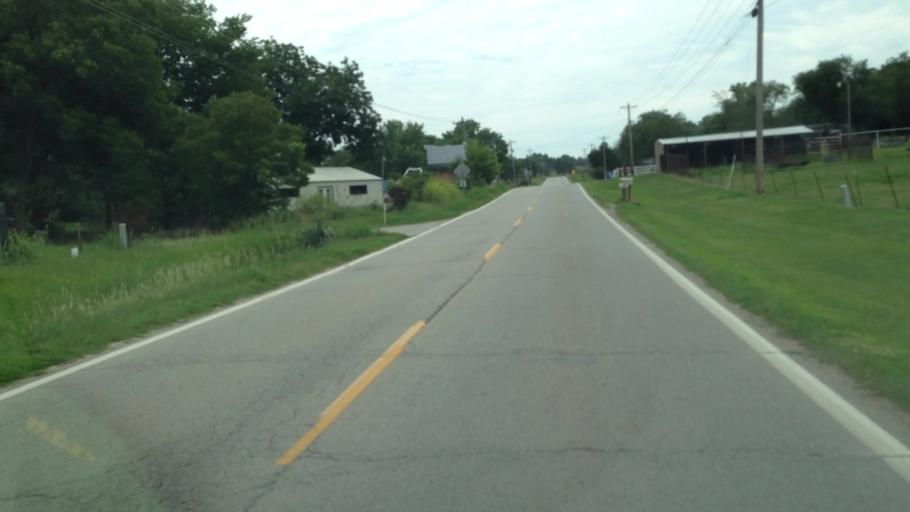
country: US
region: Oklahoma
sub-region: Delaware County
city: Cleora
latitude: 36.5765
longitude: -94.9707
